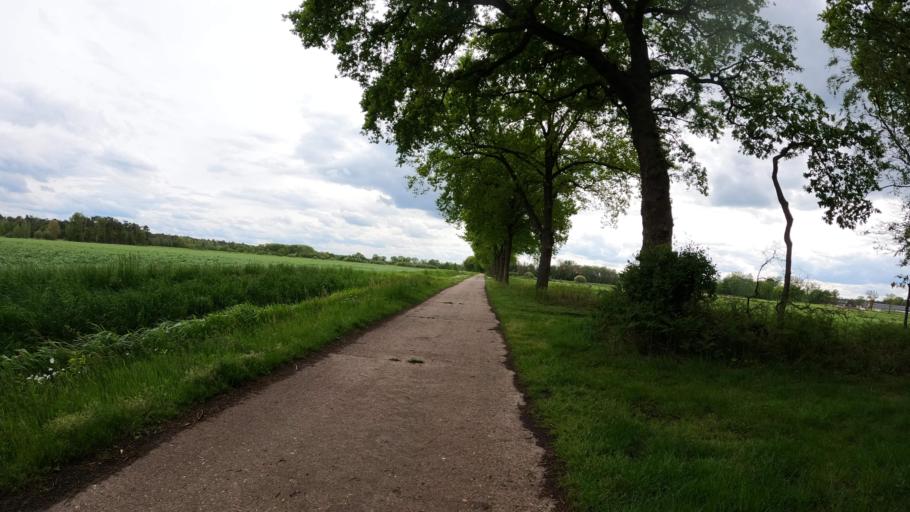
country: BE
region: Flanders
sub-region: Provincie Antwerpen
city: Vosselaar
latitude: 51.2825
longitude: 4.9083
